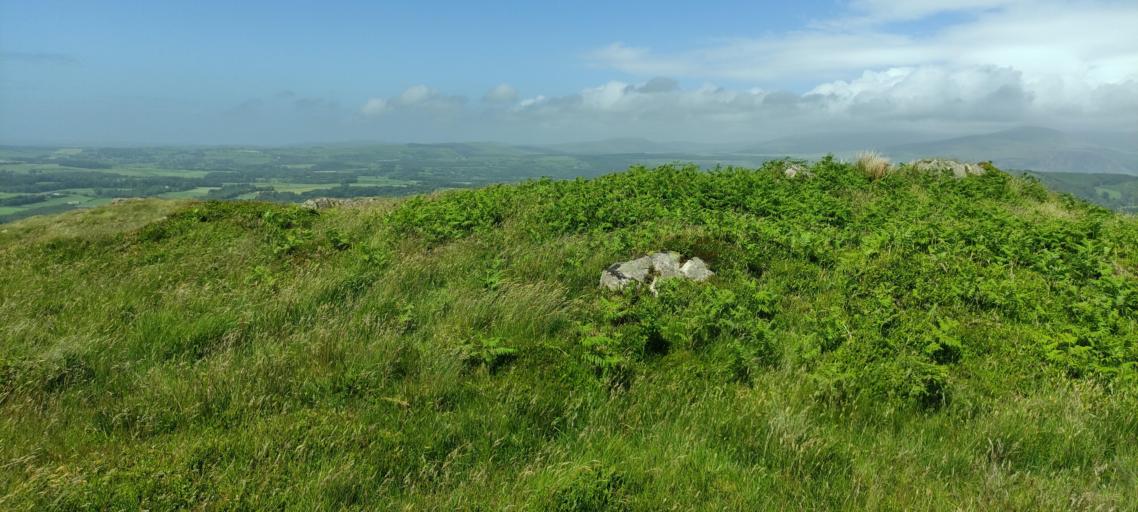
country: GB
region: England
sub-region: Cumbria
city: Seascale
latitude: 54.3727
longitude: -3.3683
